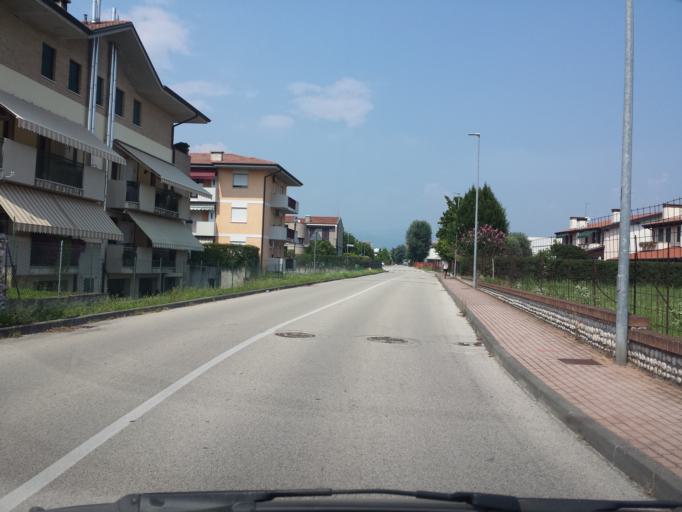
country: IT
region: Veneto
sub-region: Provincia di Vicenza
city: Sandrigo
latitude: 45.6589
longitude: 11.5956
